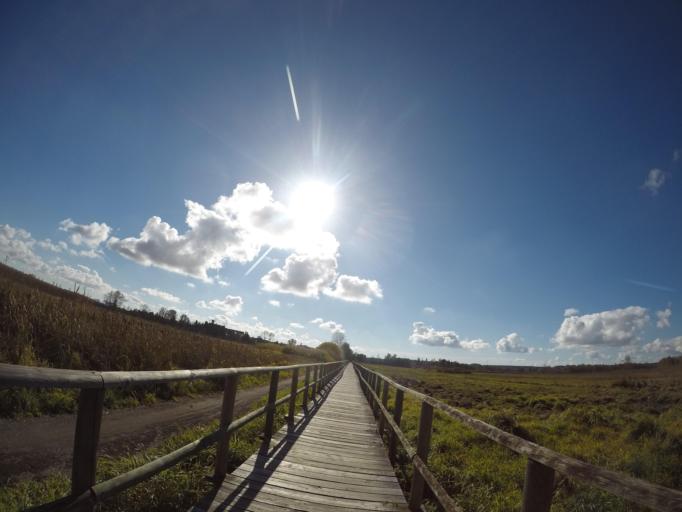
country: DE
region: Baden-Wuerttemberg
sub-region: Tuebingen Region
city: Bad Buchau
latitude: 48.0748
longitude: 9.6047
